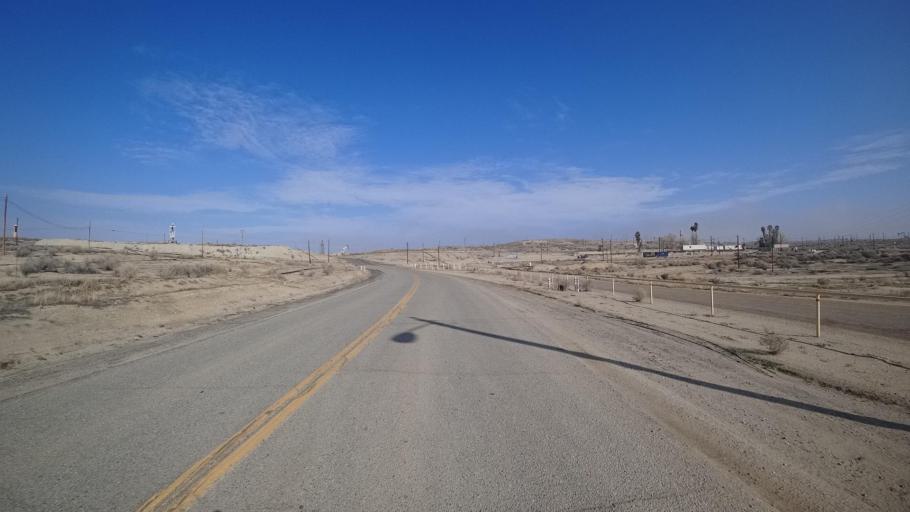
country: US
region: California
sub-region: Kern County
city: Ford City
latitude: 35.1608
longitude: -119.4216
